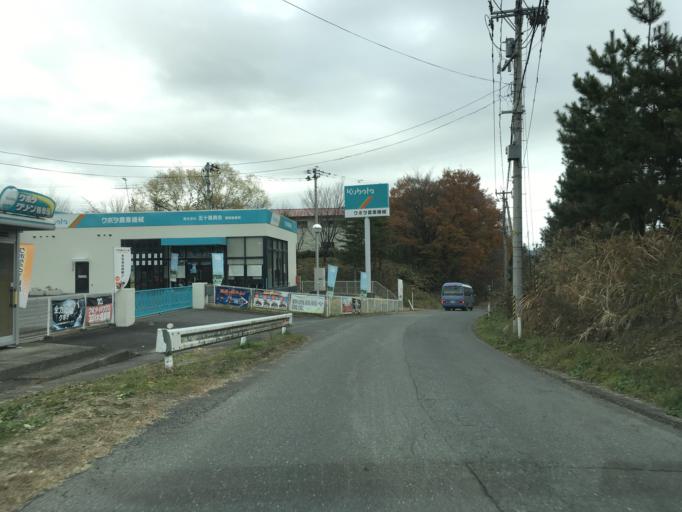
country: JP
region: Iwate
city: Ichinoseki
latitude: 38.7954
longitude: 140.9765
